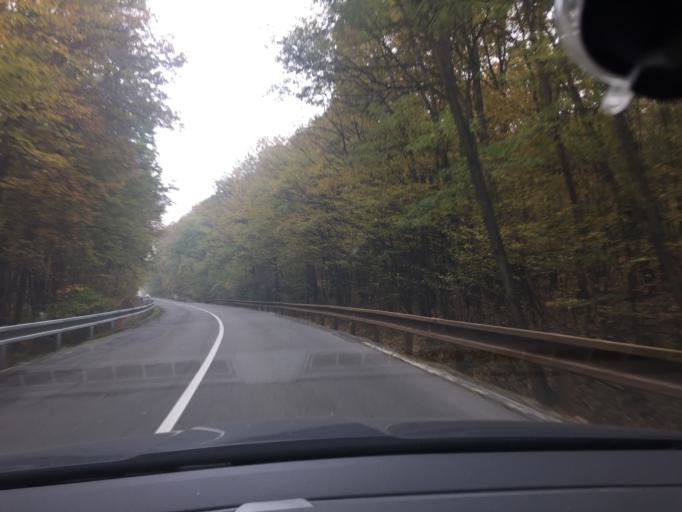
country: SK
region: Banskobystricky
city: Velky Krtis
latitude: 48.2604
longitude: 19.4251
